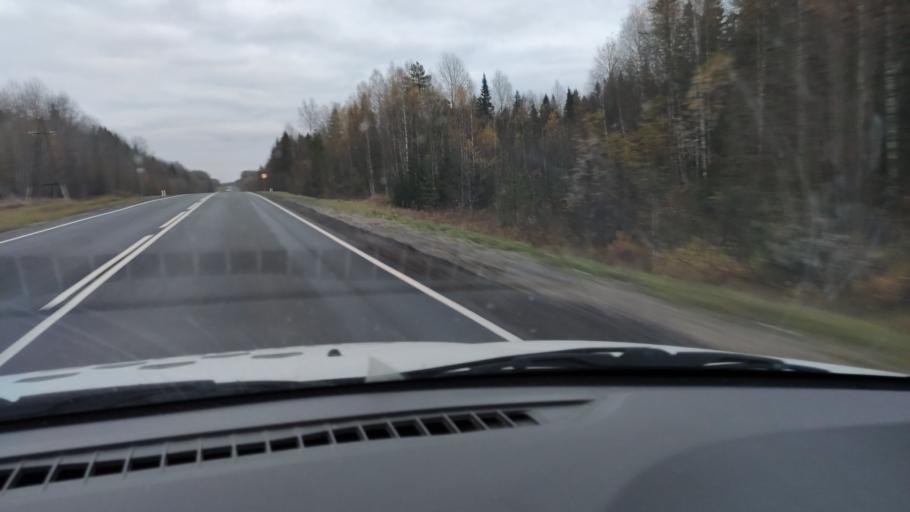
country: RU
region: Kirov
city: Lesnyye Polyany
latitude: 58.8011
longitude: 52.5473
